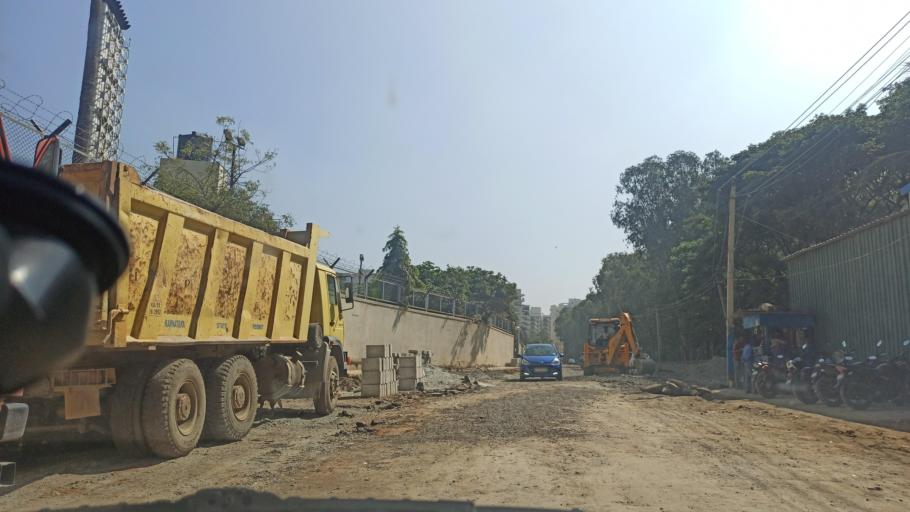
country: IN
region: Karnataka
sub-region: Bangalore Urban
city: Bangalore
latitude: 12.9186
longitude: 77.6860
